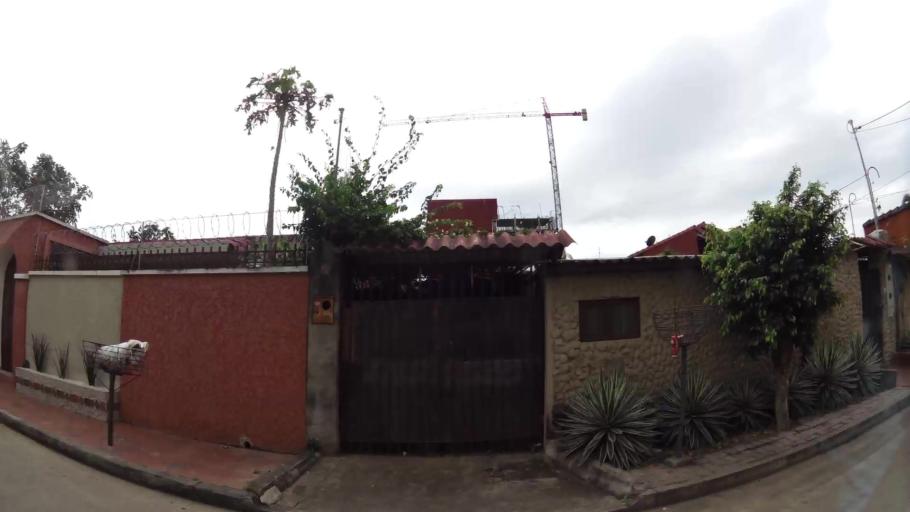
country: BO
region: Santa Cruz
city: Santa Cruz de la Sierra
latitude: -17.7677
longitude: -63.2052
